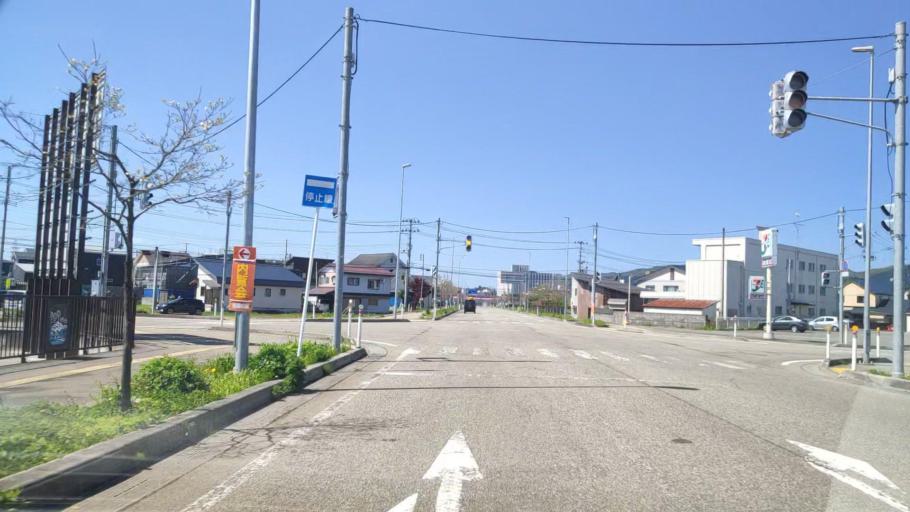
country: JP
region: Akita
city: Omagari
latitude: 39.4689
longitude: 140.4836
